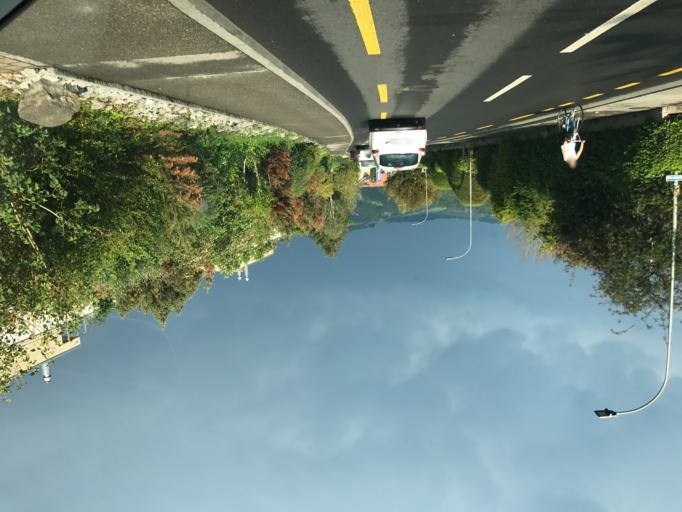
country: CH
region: Bern
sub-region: Thun District
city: Thun
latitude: 46.7452
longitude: 7.6181
